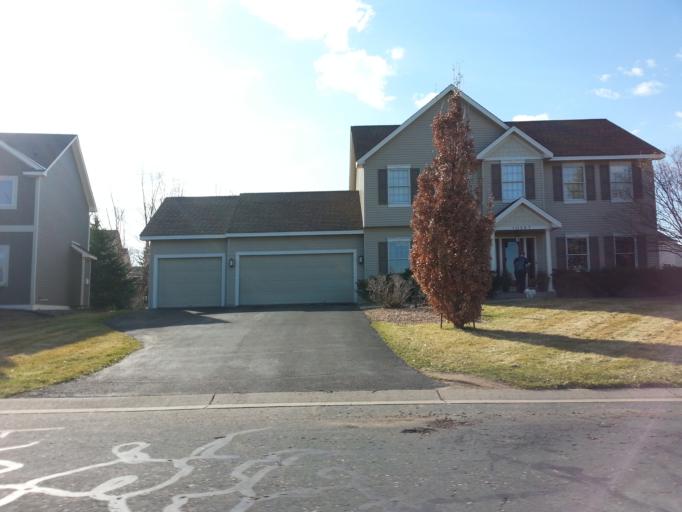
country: US
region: Minnesota
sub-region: Washington County
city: Woodbury
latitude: 44.8946
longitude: -92.8974
